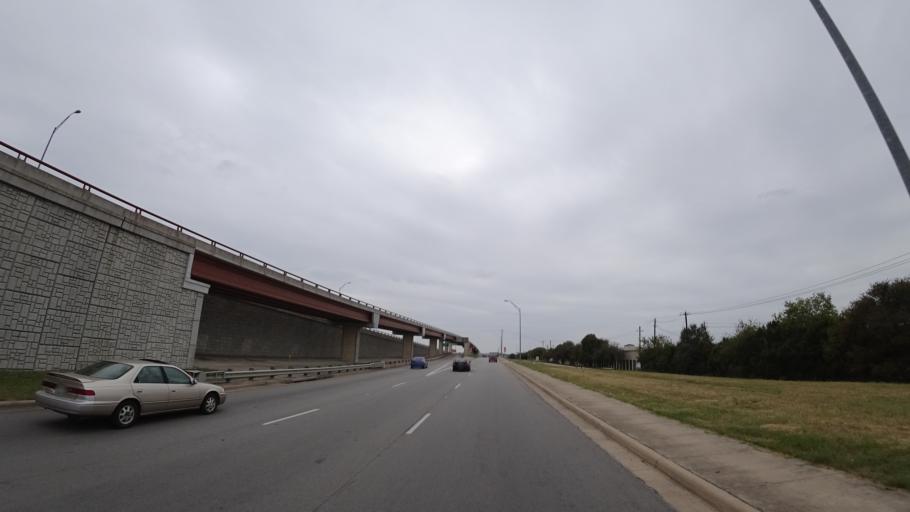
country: US
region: Texas
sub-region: Travis County
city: Wells Branch
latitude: 30.4287
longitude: -97.7020
